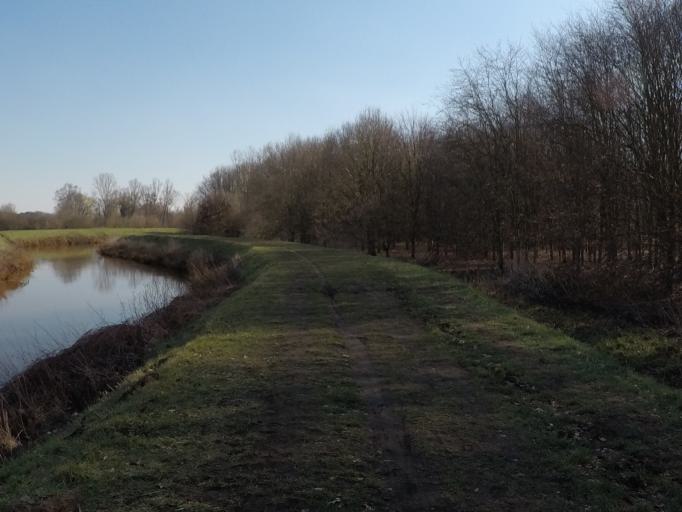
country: BE
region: Flanders
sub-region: Provincie Antwerpen
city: Herenthout
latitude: 51.1119
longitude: 4.7329
